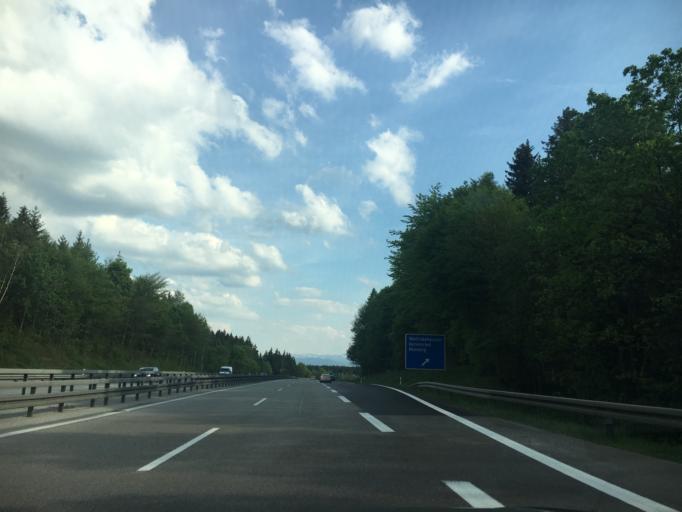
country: DE
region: Bavaria
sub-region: Upper Bavaria
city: Wolfratshausen
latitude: 47.9076
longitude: 11.3953
